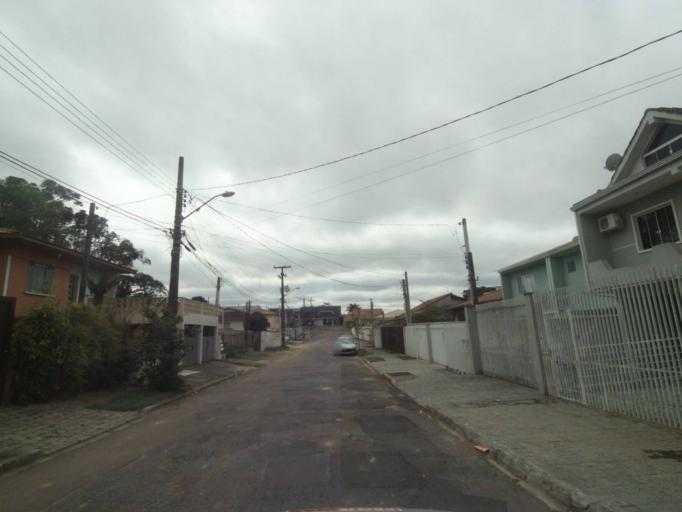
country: BR
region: Parana
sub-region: Pinhais
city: Pinhais
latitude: -25.4812
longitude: -49.2268
